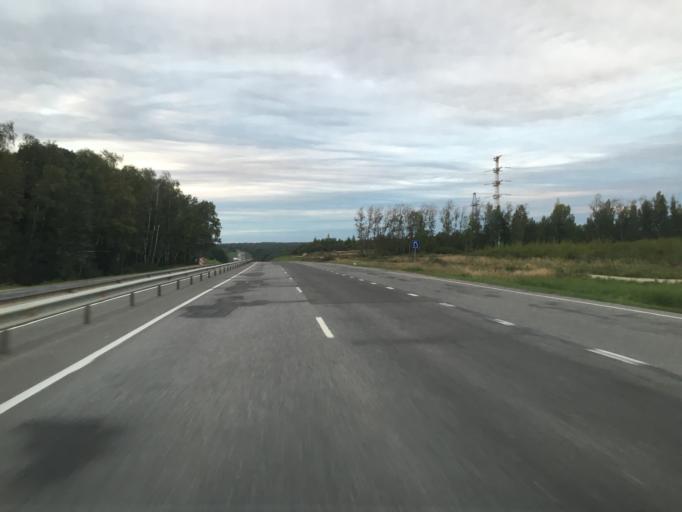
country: RU
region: Kaluga
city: Kaluga
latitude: 54.5894
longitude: 36.3308
